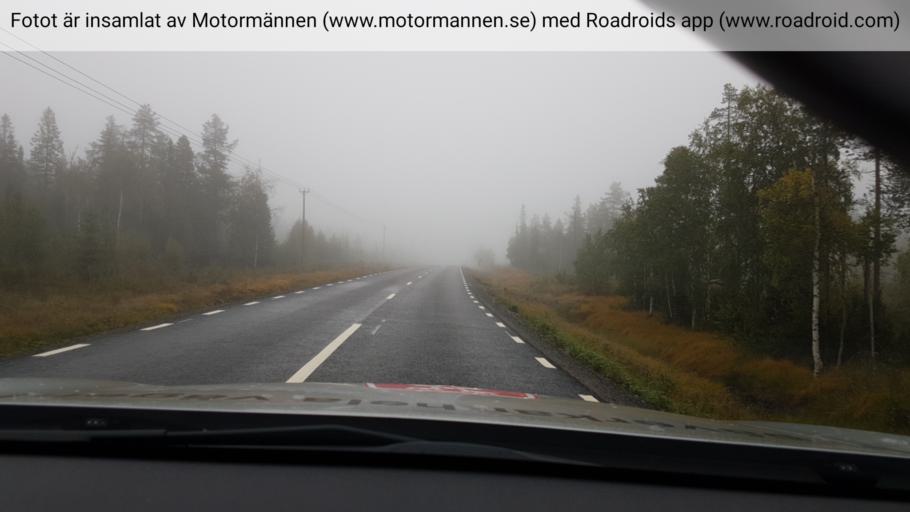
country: SE
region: Vaesterbotten
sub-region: Umea Kommun
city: Ersmark
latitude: 64.2497
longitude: 20.3077
